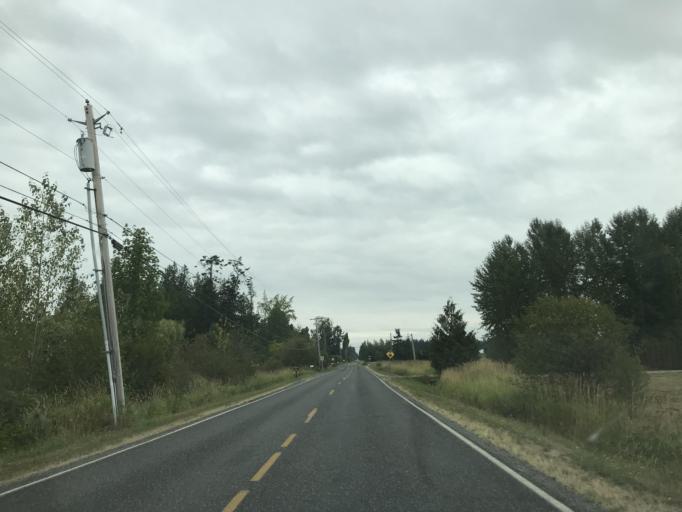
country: US
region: Washington
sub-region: Whatcom County
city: Everson
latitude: 48.8306
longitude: -122.3325
